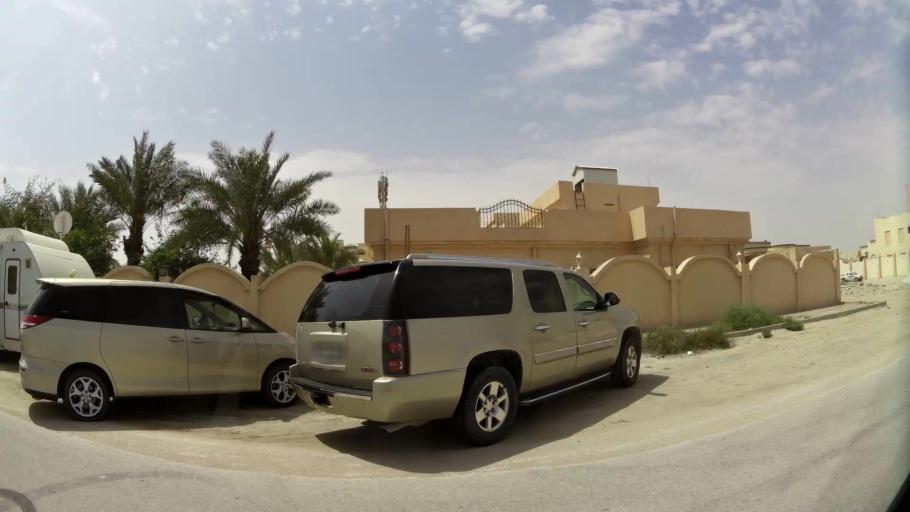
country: QA
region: Baladiyat ar Rayyan
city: Ar Rayyan
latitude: 25.3549
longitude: 51.4764
